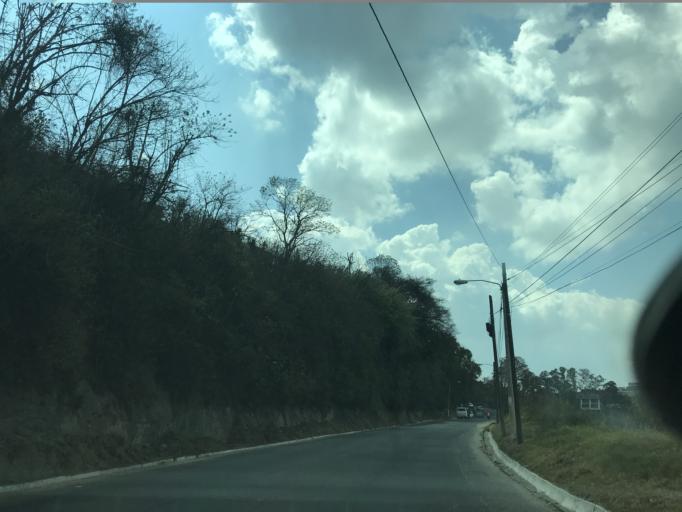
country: GT
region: Guatemala
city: Mixco
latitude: 14.6756
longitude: -90.5730
